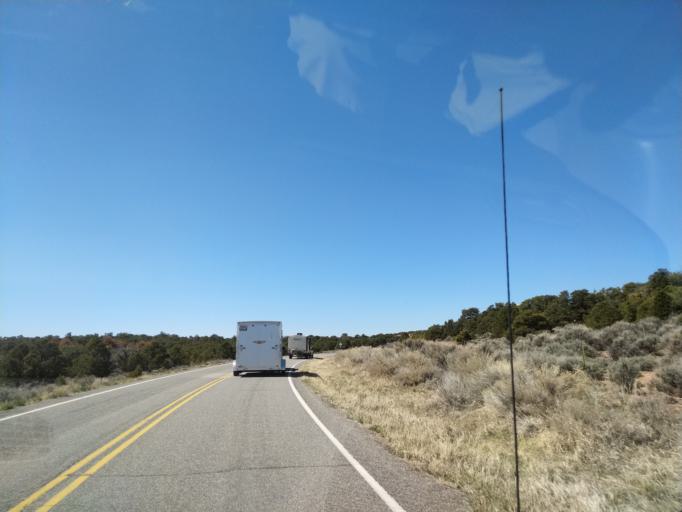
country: US
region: Colorado
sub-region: Mesa County
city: Redlands
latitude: 39.0109
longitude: -108.6739
